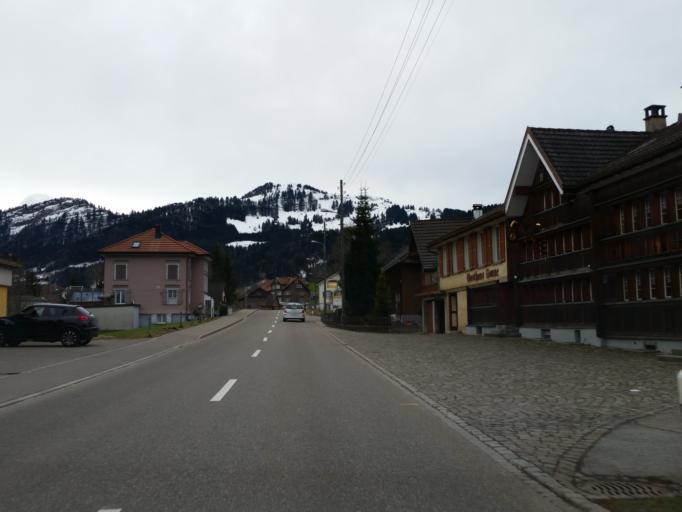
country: CH
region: Appenzell Ausserrhoden
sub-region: Bezirk Hinterland
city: Urnasch
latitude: 47.3065
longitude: 9.2753
